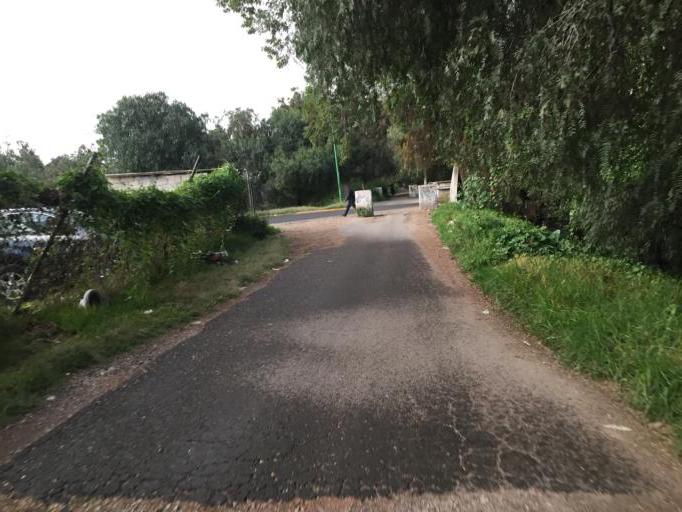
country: MX
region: Mexico
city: Cuautitlan Izcalli
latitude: 19.6719
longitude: -99.2176
